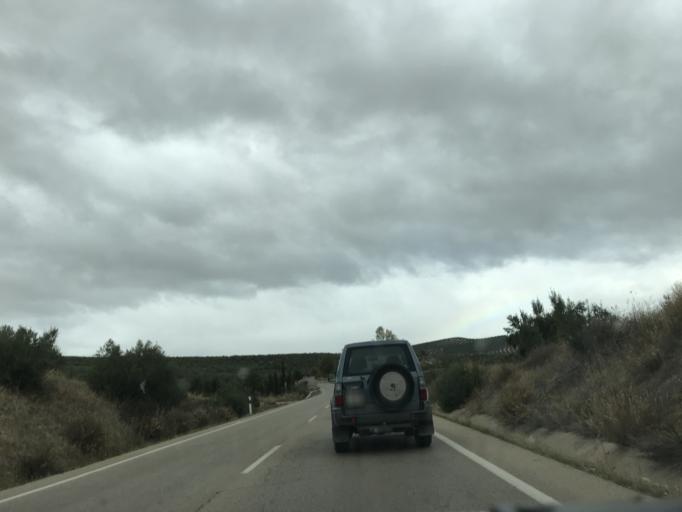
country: ES
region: Andalusia
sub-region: Provincia de Jaen
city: Peal de Becerro
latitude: 37.9241
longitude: -3.1363
